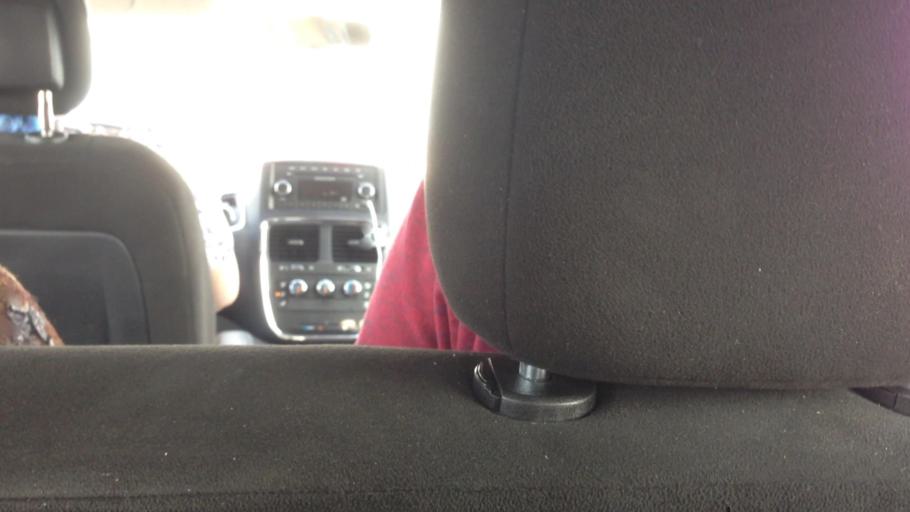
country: US
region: New York
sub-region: Ulster County
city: Lake Katrine
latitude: 41.9807
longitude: -73.9544
